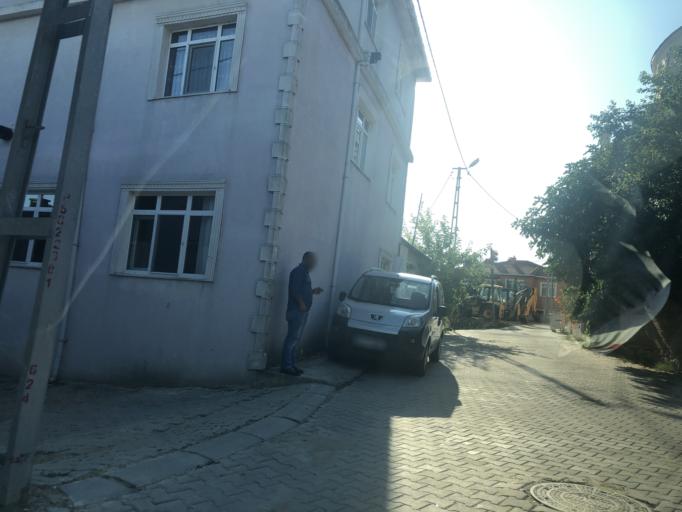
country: TR
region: Istanbul
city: Catalca
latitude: 41.2239
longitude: 28.4765
